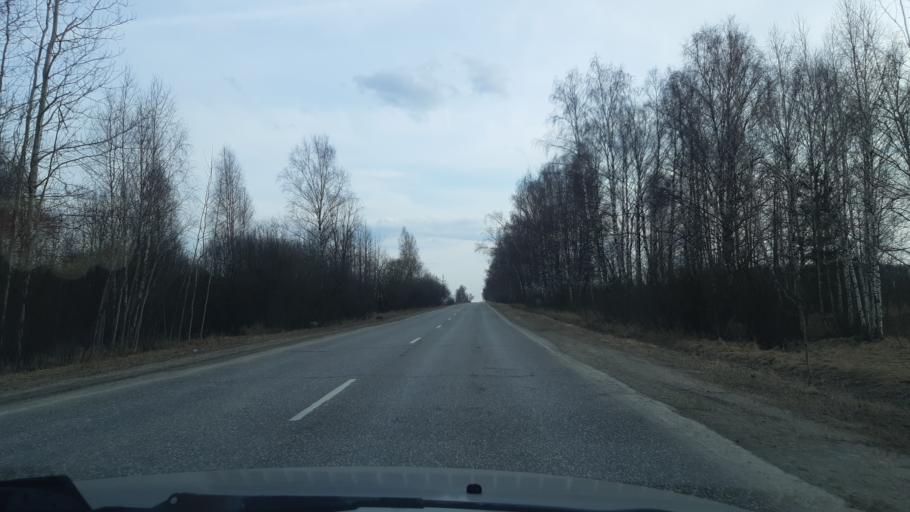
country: RU
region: Vladimir
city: Luknovo
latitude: 56.2077
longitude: 42.0327
